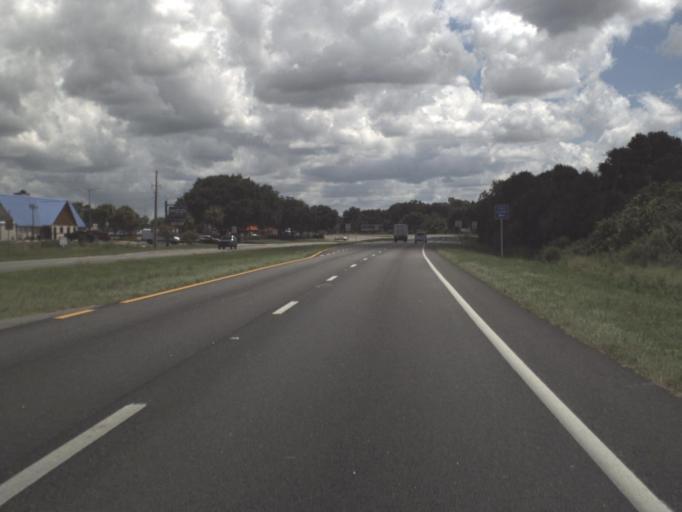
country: US
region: Florida
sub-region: Polk County
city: Lake Wales
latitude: 27.9008
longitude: -81.6070
